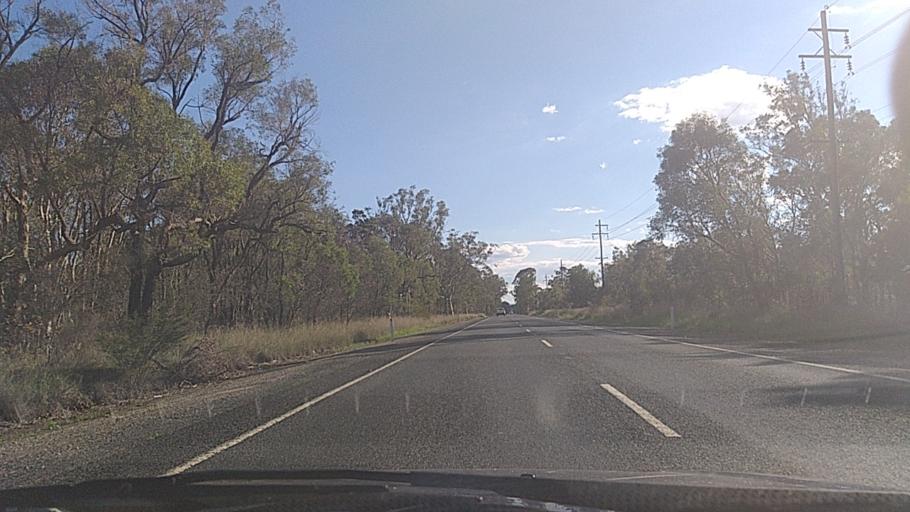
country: AU
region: New South Wales
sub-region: Penrith Municipality
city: Werrington Downs
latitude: -33.6751
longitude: 150.7477
